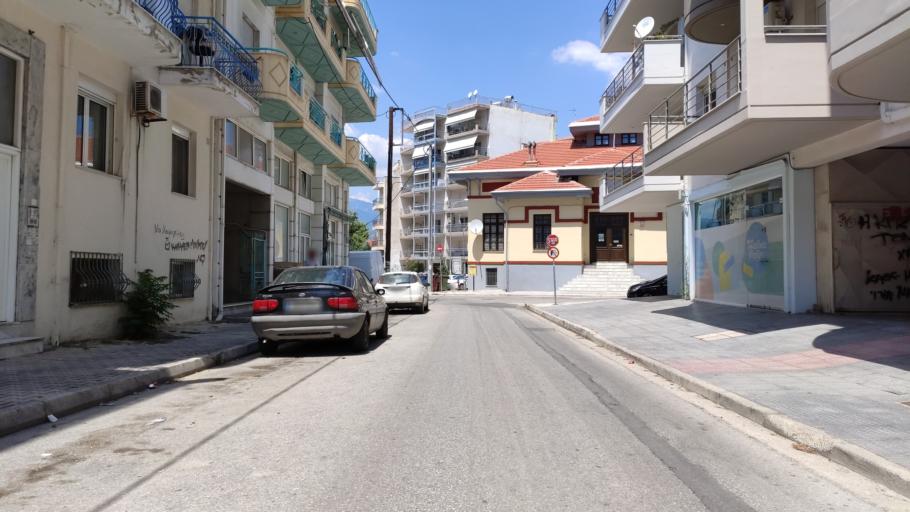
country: GR
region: East Macedonia and Thrace
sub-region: Nomos Rodopis
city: Komotini
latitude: 41.1191
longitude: 25.3962
